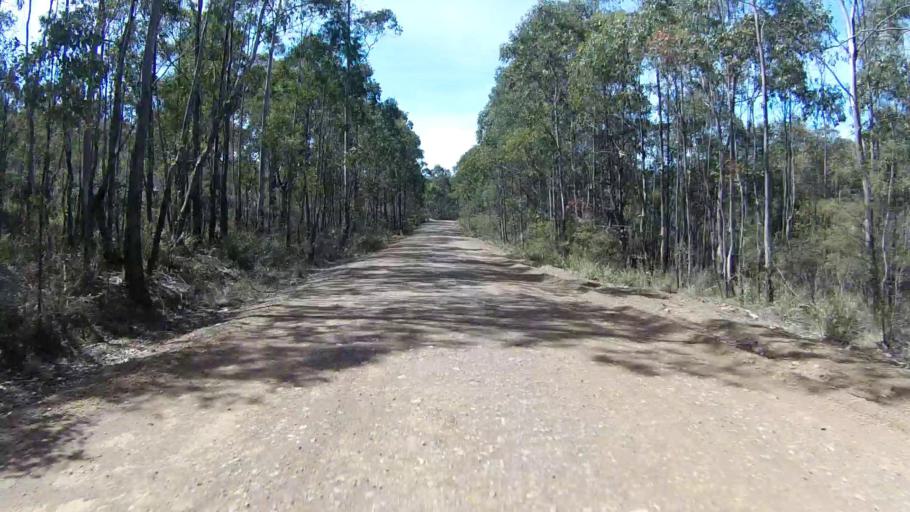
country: AU
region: Tasmania
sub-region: Sorell
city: Sorell
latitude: -42.6737
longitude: 147.7273
